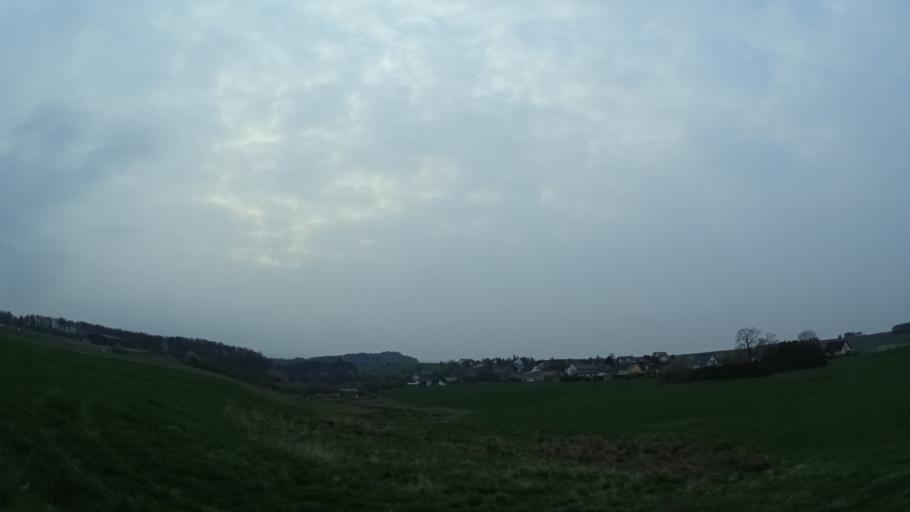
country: DE
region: Rheinland-Pfalz
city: Schmissberg
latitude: 49.6584
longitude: 7.2046
